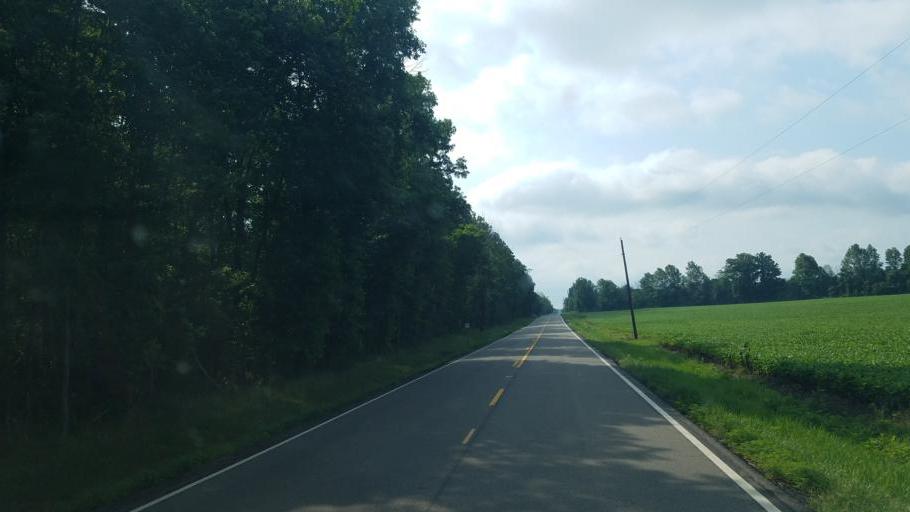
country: US
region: Ohio
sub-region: Knox County
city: Centerburg
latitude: 40.2606
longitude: -82.5993
